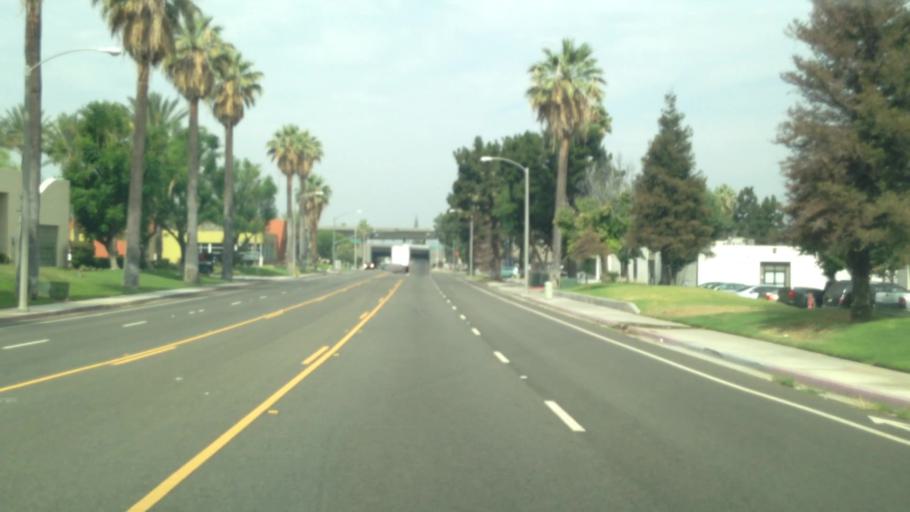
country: US
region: California
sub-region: Riverside County
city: Highgrove
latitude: 33.9903
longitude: -117.3465
